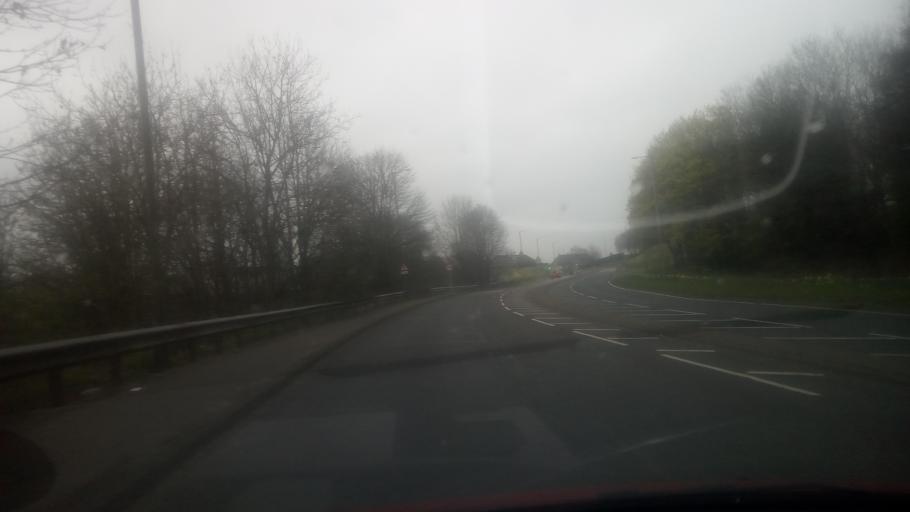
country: GB
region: Scotland
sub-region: Stirling
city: Stirling
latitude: 56.1060
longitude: -3.9321
